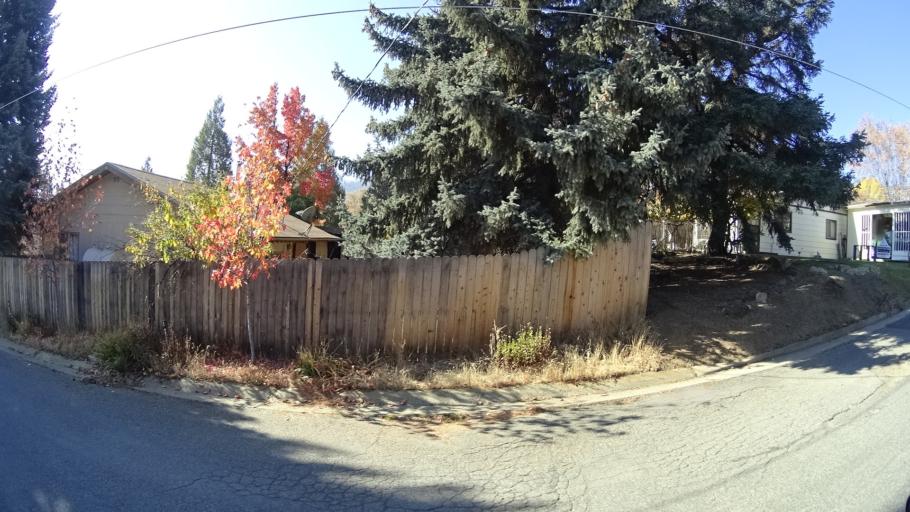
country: US
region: California
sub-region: Siskiyou County
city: Yreka
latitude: 41.7393
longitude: -122.6537
